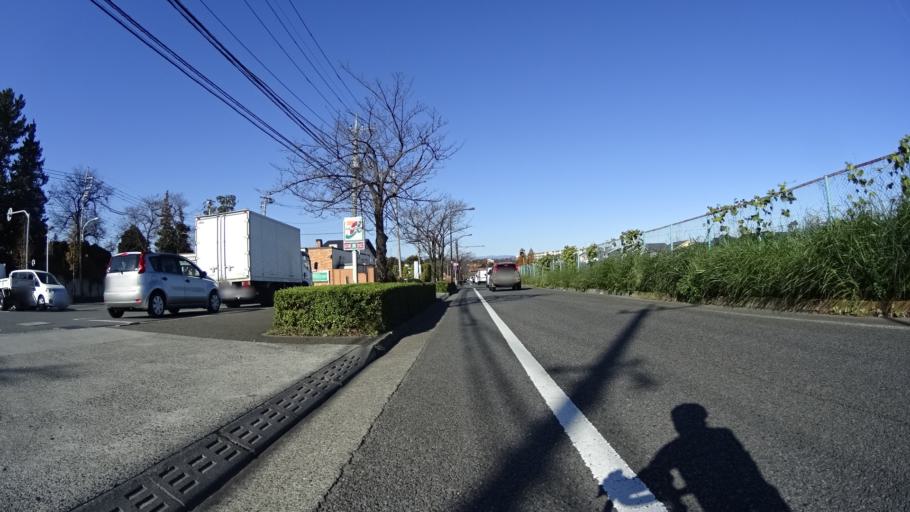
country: JP
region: Tokyo
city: Hino
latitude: 35.6100
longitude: 139.4204
